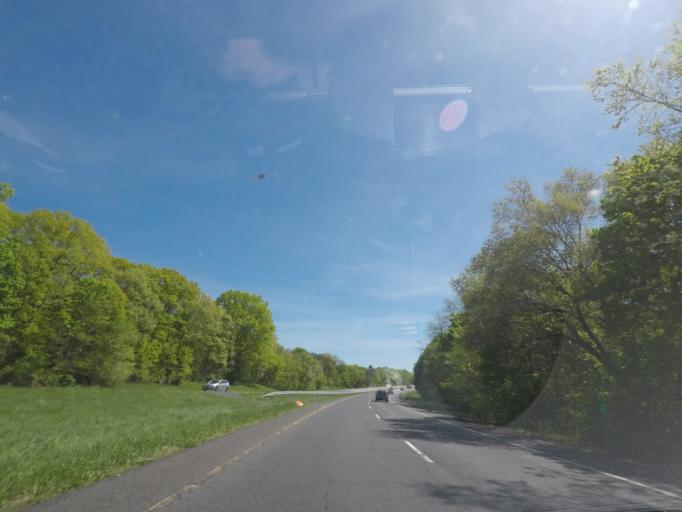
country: US
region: New York
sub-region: Ulster County
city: Lincoln Park
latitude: 41.9409
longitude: -73.9831
